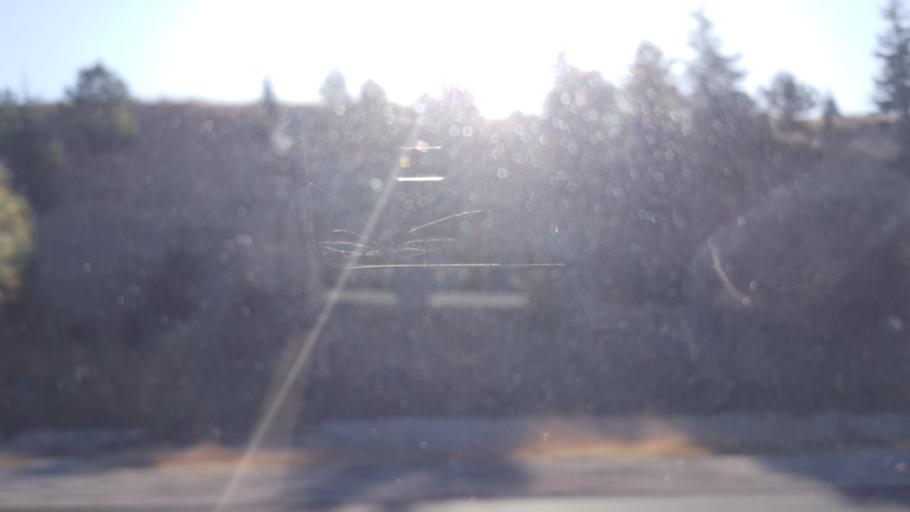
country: TR
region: Ankara
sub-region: Goelbasi
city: Golbasi
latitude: 39.8314
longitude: 32.8856
